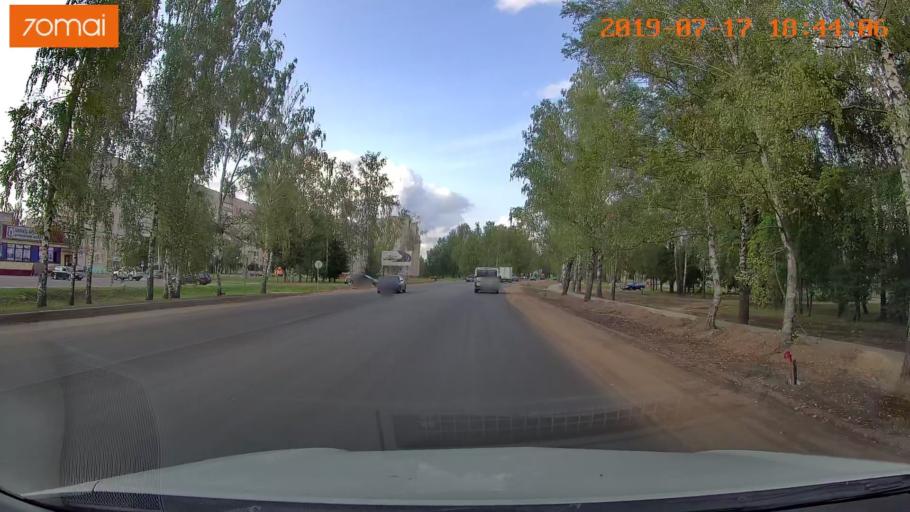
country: BY
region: Mogilev
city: Asipovichy
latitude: 53.3185
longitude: 28.6463
